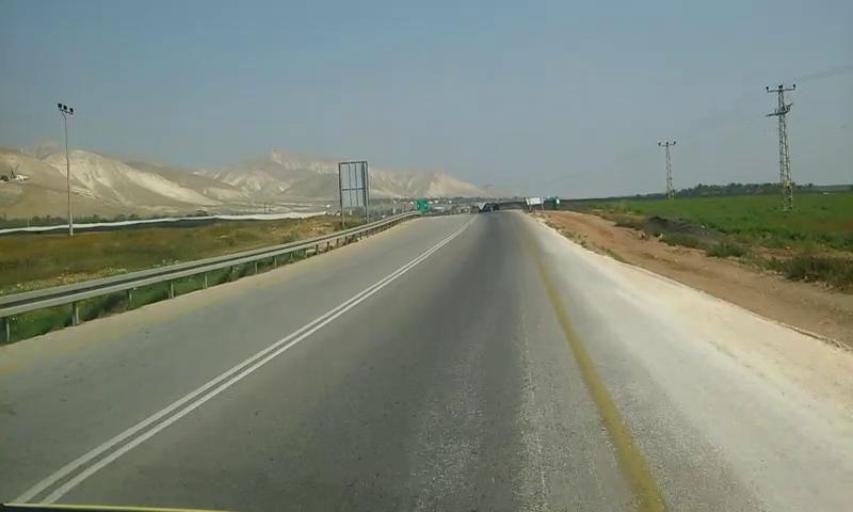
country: PS
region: West Bank
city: Al Fasayil
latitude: 32.0455
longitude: 35.4626
